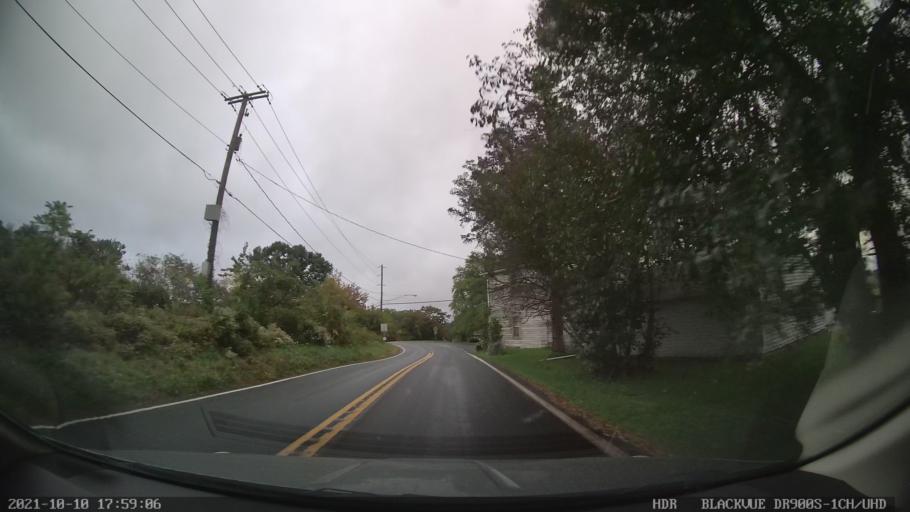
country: US
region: Pennsylvania
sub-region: Lehigh County
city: Schnecksville
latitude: 40.6354
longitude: -75.5638
